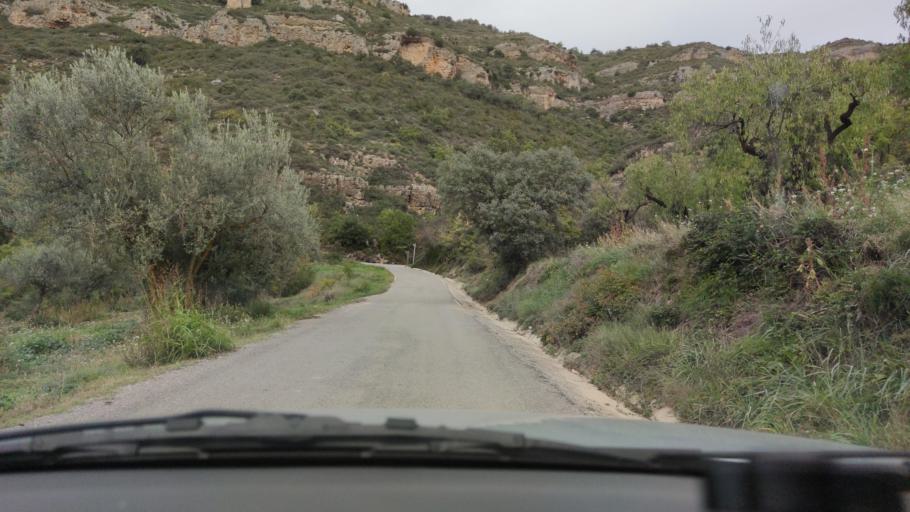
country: ES
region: Catalonia
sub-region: Provincia de Lleida
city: Llimiana
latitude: 42.0699
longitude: 0.9411
